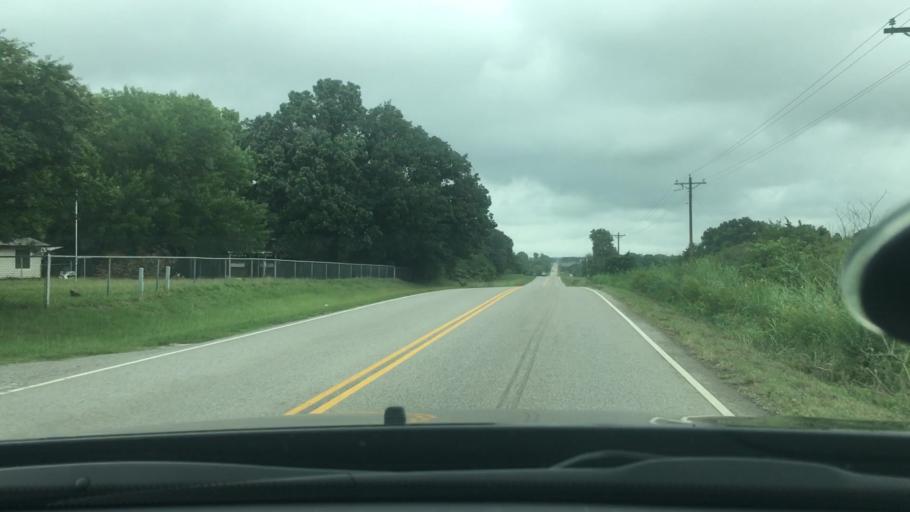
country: US
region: Oklahoma
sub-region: Bryan County
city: Calera
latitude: 33.9502
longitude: -96.5004
